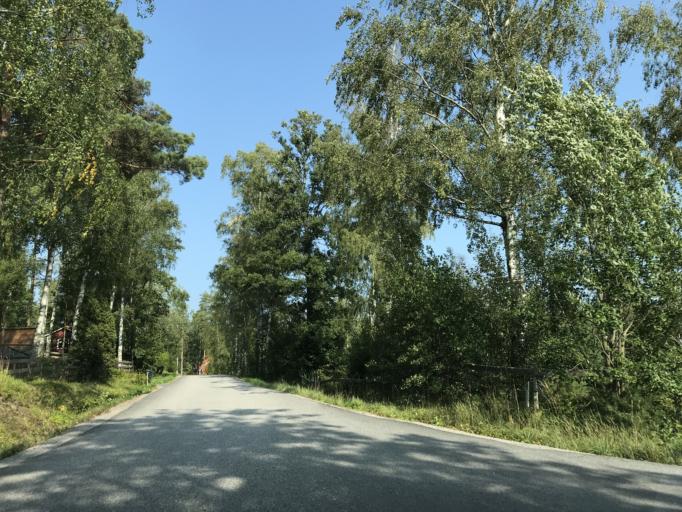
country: SE
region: Stockholm
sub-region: Norrtalje Kommun
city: Bjorko
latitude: 59.8611
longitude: 19.0341
